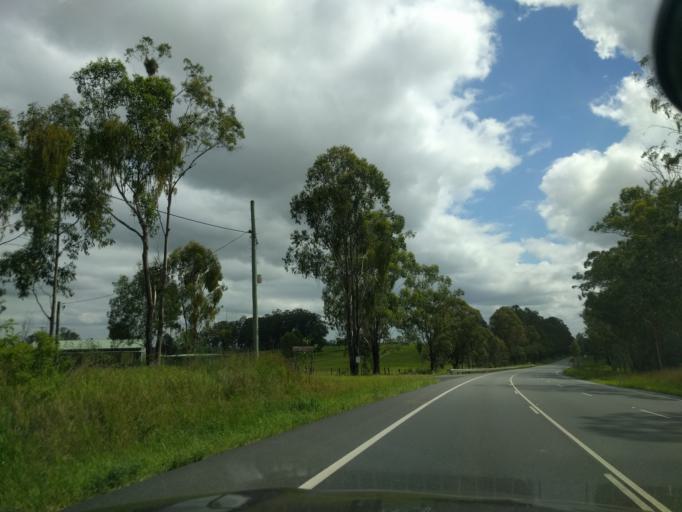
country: AU
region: Queensland
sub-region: Logan
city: Cedar Vale
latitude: -27.8760
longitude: 152.9917
